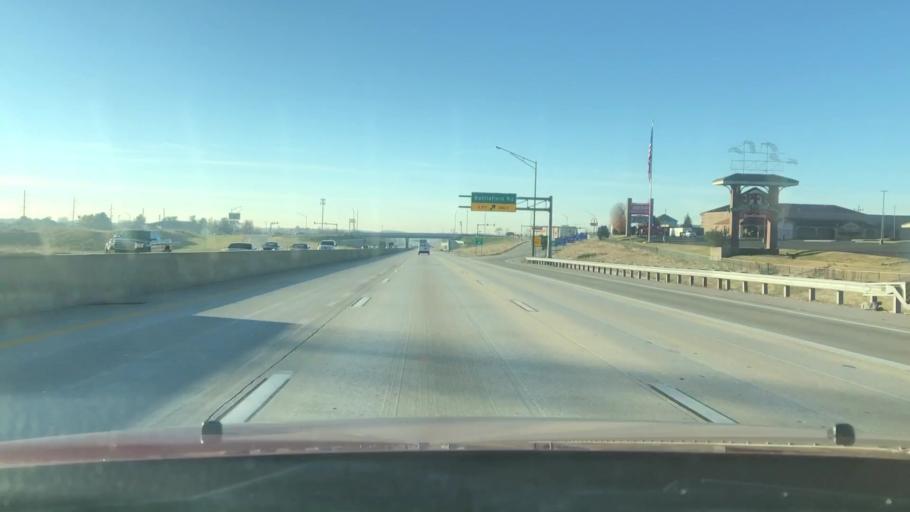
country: US
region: Missouri
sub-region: Greene County
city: Springfield
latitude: 37.1617
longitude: -93.2247
